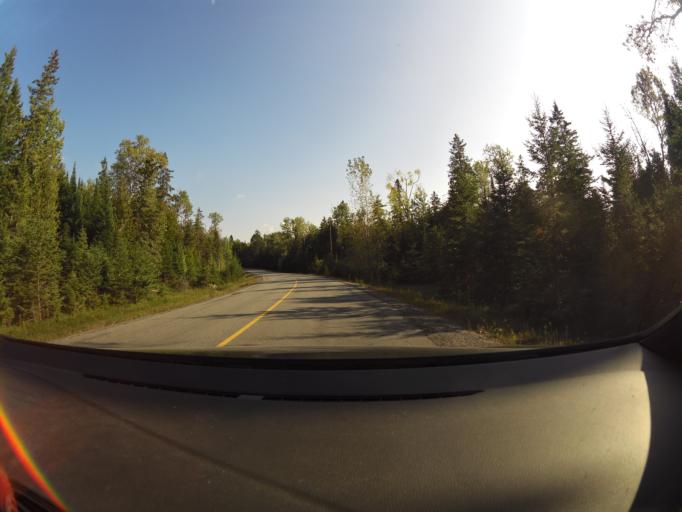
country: CA
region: Ontario
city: Arnprior
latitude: 45.4448
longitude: -76.2776
